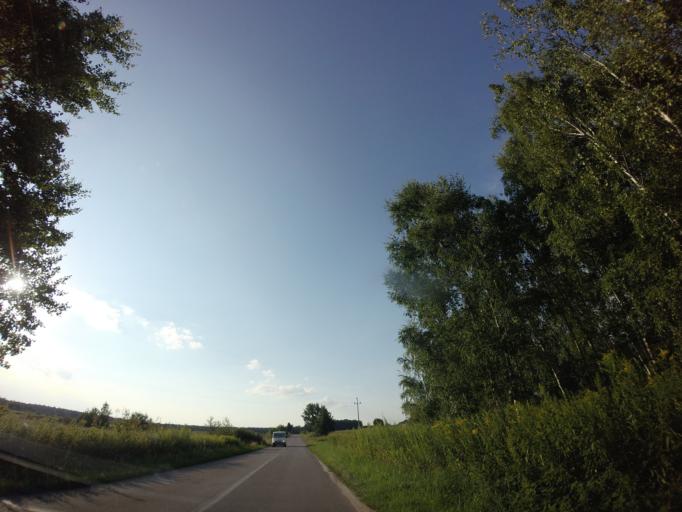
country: PL
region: Lublin Voivodeship
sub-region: Powiat pulawski
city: Kurow
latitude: 51.4166
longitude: 22.2003
